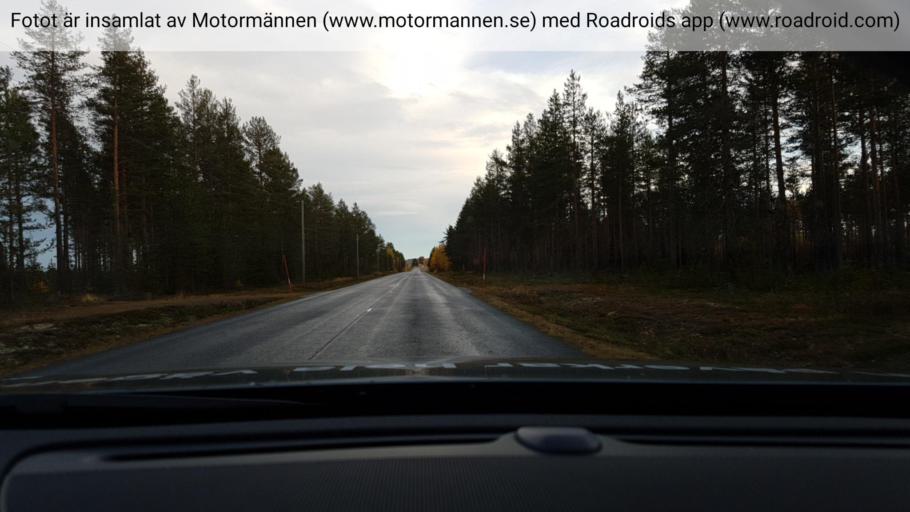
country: SE
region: Norrbotten
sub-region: Overkalix Kommun
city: OEverkalix
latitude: 66.9442
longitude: 22.7213
